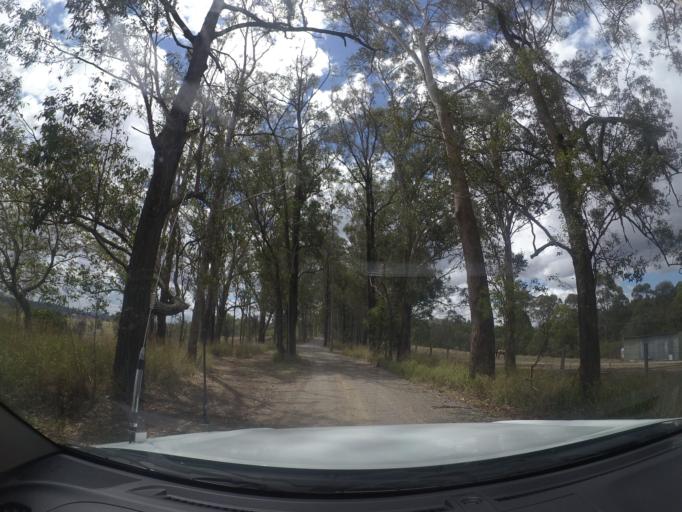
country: AU
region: Queensland
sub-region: Logan
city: Cedar Vale
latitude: -27.9147
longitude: 153.0310
